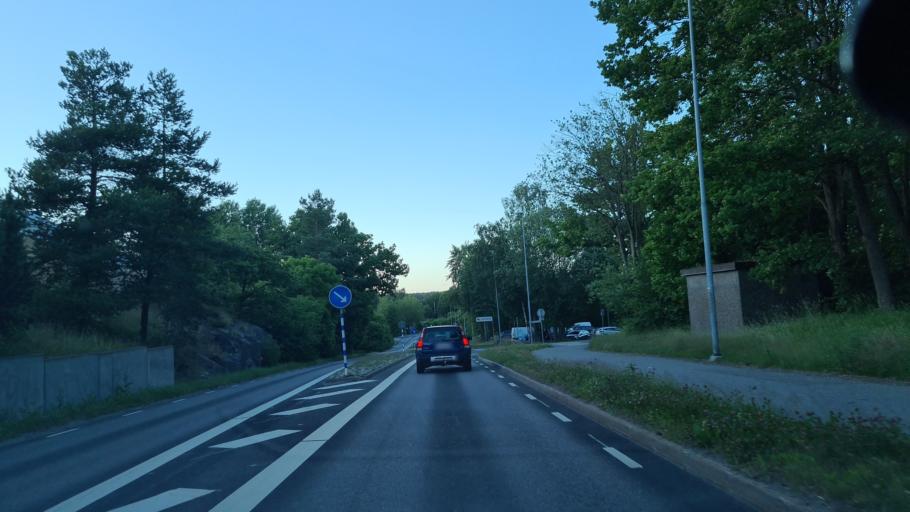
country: SE
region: Stockholm
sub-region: Nacka Kommun
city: Alta
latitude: 59.2538
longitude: 18.1778
